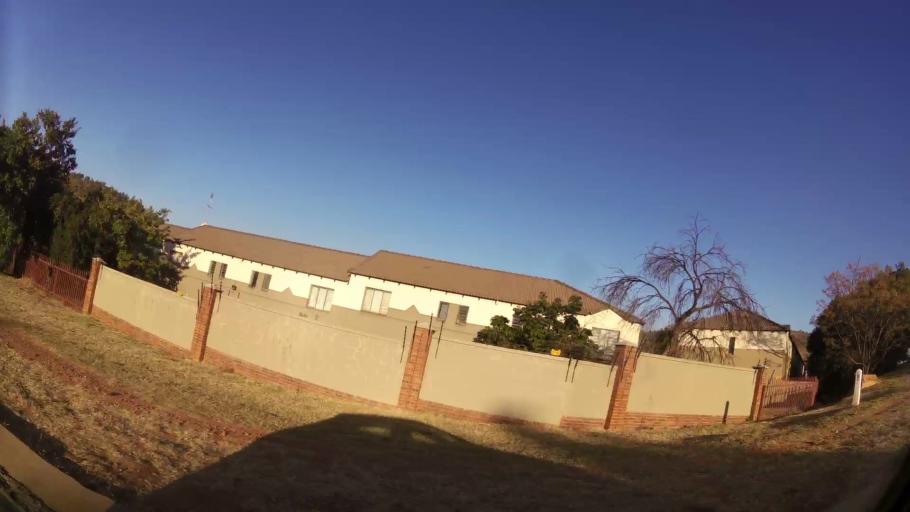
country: ZA
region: North-West
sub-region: Bojanala Platinum District Municipality
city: Rustenburg
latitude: -25.7123
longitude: 27.2404
